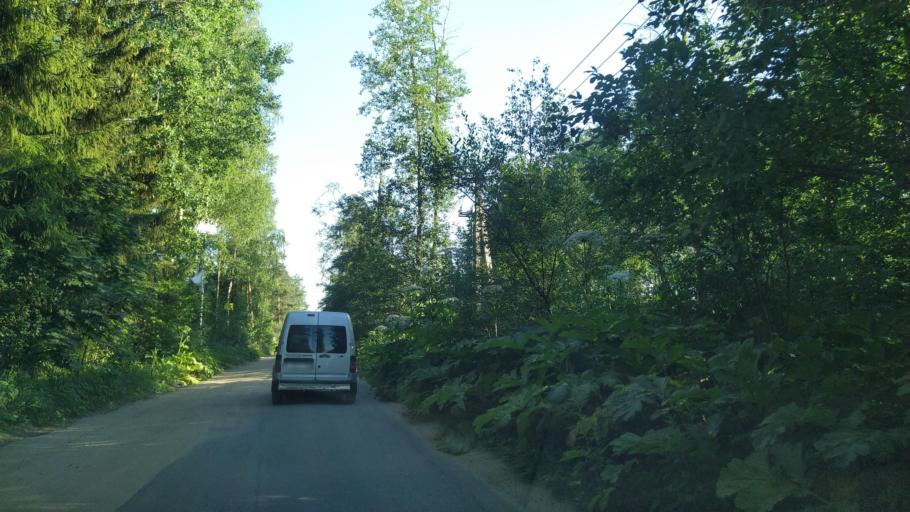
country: RU
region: Leningrad
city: Koltushi
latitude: 59.9029
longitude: 30.7339
